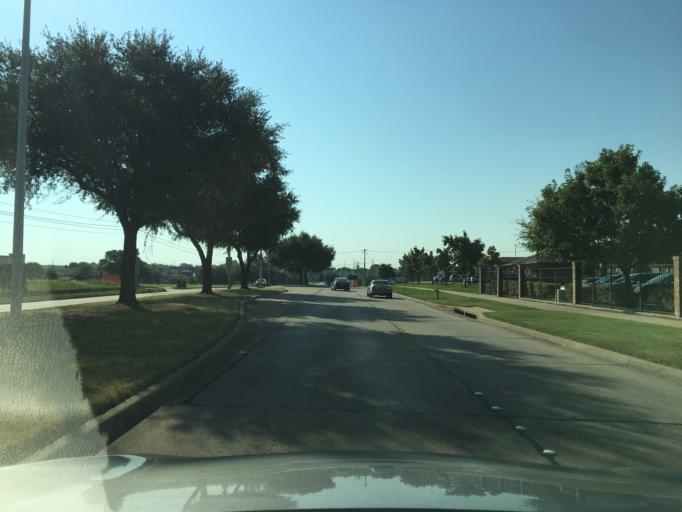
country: US
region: Texas
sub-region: Dallas County
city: Garland
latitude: 32.9511
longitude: -96.6531
